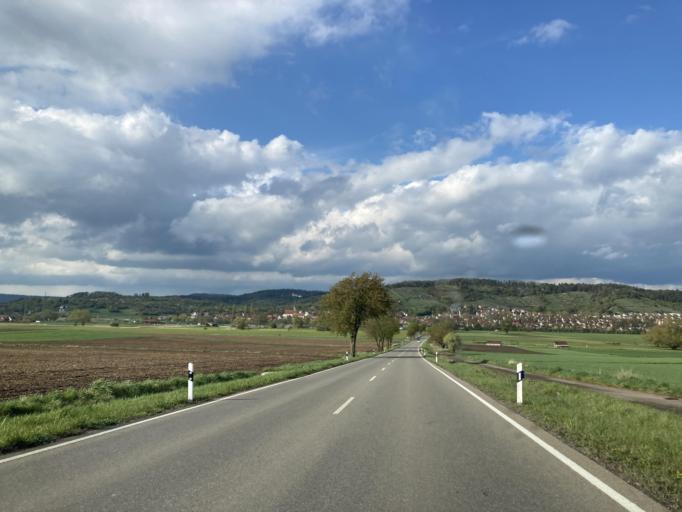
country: DE
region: Baden-Wuerttemberg
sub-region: Tuebingen Region
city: Rottenburg
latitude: 48.5154
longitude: 8.9741
